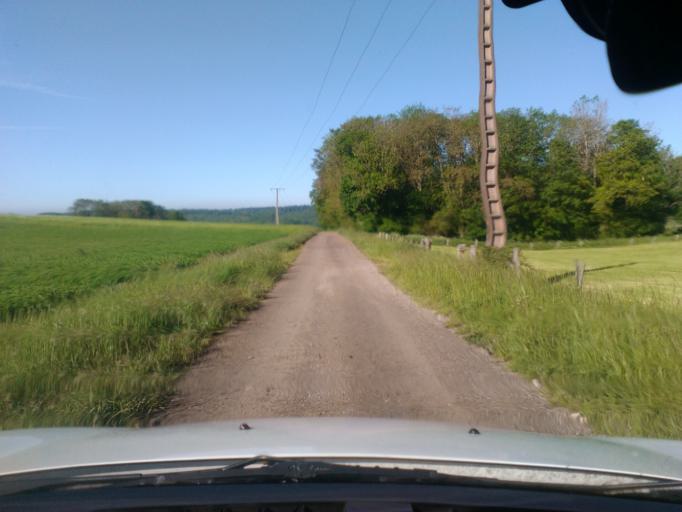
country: FR
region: Lorraine
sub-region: Departement des Vosges
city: Mirecourt
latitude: 48.3257
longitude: 6.2096
